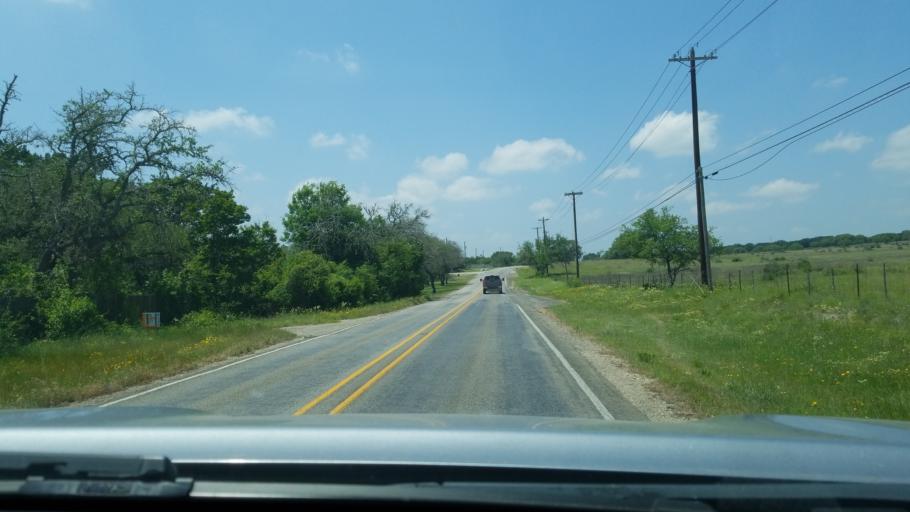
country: US
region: Texas
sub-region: Hays County
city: Woodcreek
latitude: 30.0358
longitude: -98.1810
